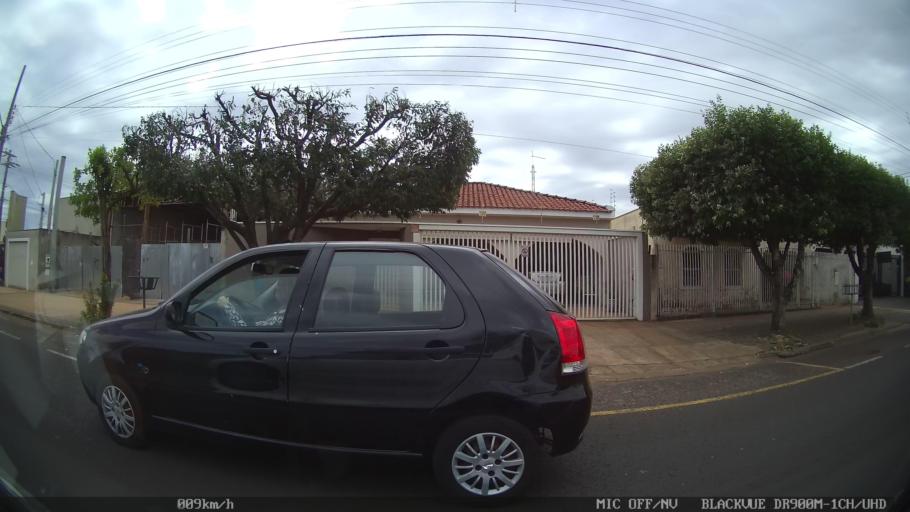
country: BR
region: Sao Paulo
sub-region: Bady Bassitt
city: Bady Bassitt
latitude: -20.8128
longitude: -49.5025
